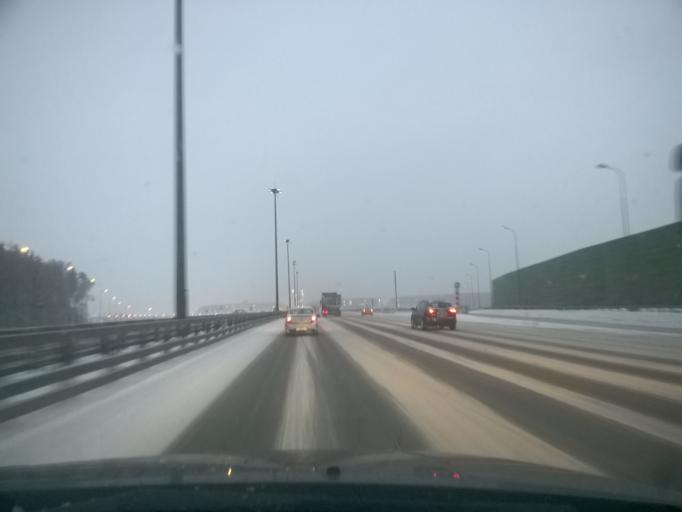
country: RU
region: Moskovskaya
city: Annino
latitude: 55.5815
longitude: 37.2459
